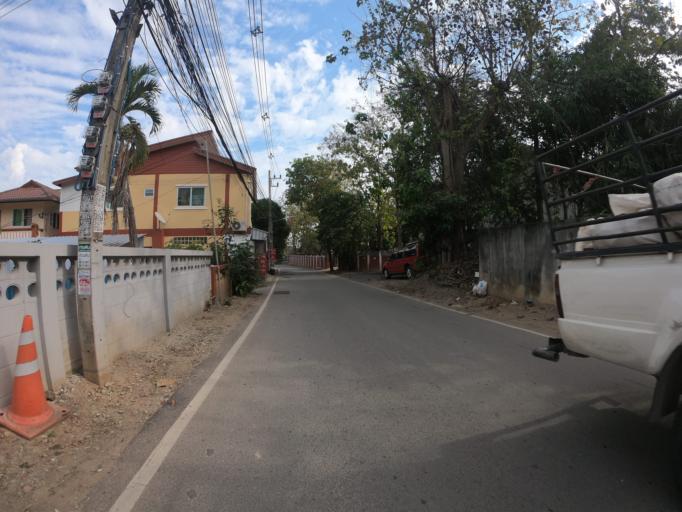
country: TH
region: Chiang Mai
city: Chiang Mai
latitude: 18.7632
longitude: 98.9425
